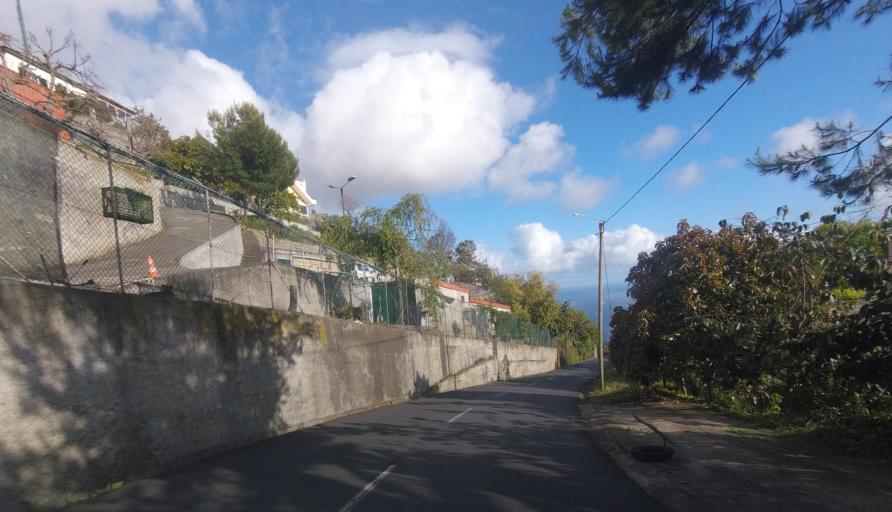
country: PT
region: Madeira
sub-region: Funchal
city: Nossa Senhora do Monte
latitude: 32.6692
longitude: -16.9028
